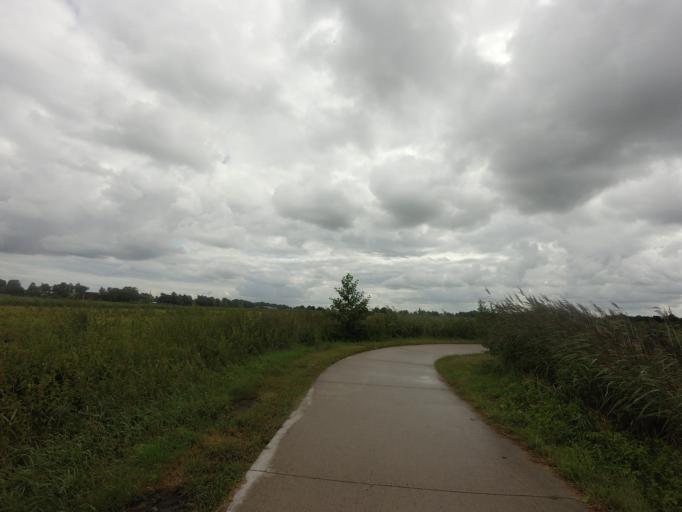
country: NL
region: Overijssel
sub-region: Gemeente Steenwijkerland
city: Wanneperveen
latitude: 52.7156
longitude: 6.1307
